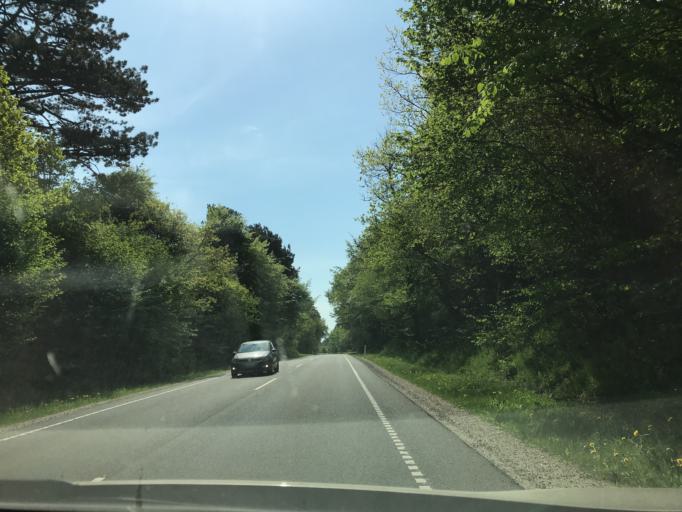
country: DK
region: South Denmark
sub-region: Middelfart Kommune
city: Ejby
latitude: 55.3943
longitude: 9.9090
